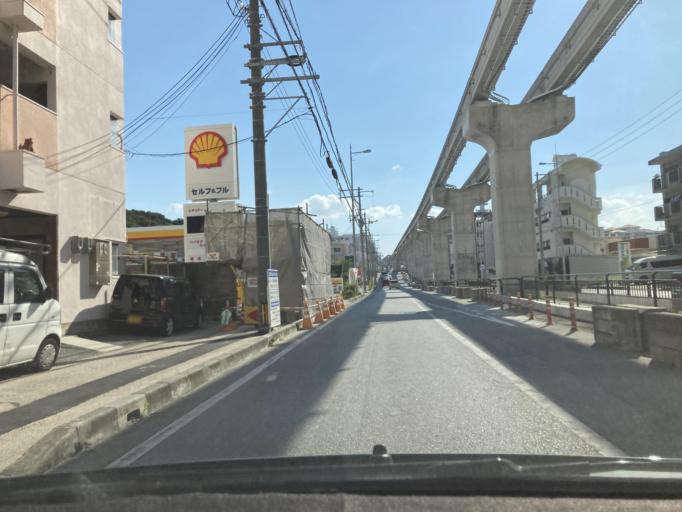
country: JP
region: Okinawa
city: Naha-shi
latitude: 26.2257
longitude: 127.7286
